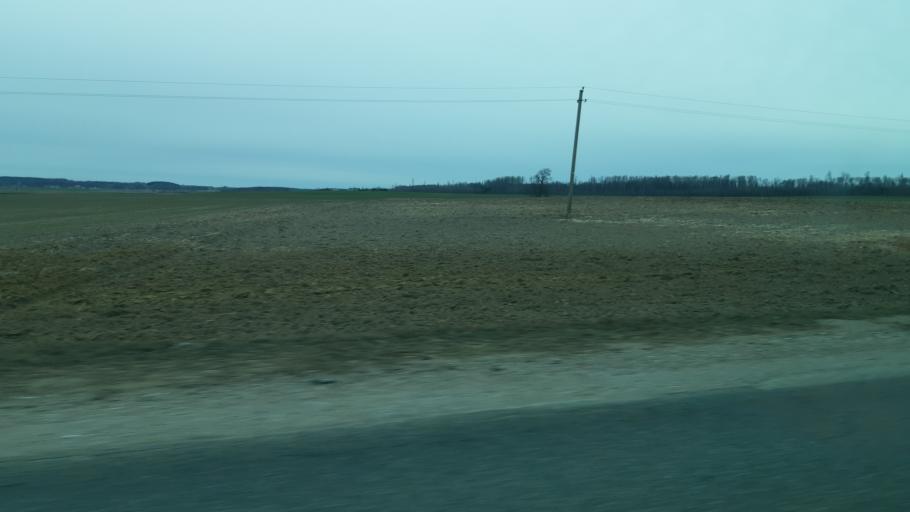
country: LT
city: Kalvarija
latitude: 54.4118
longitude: 23.1900
